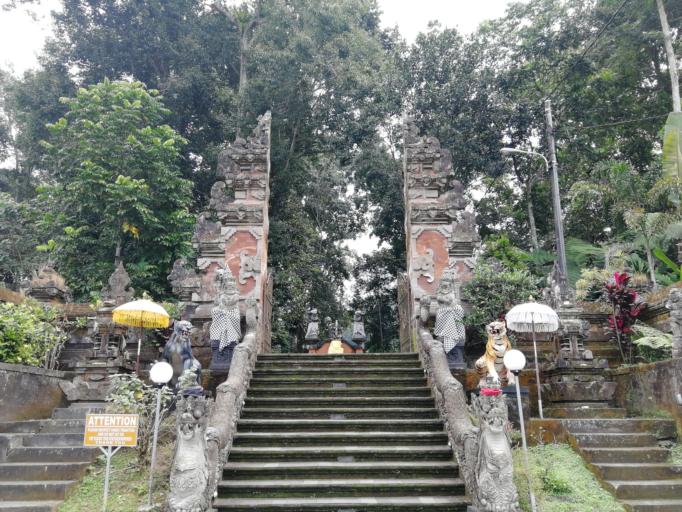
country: ID
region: Bali
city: Empalan
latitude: -8.3779
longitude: 115.1437
